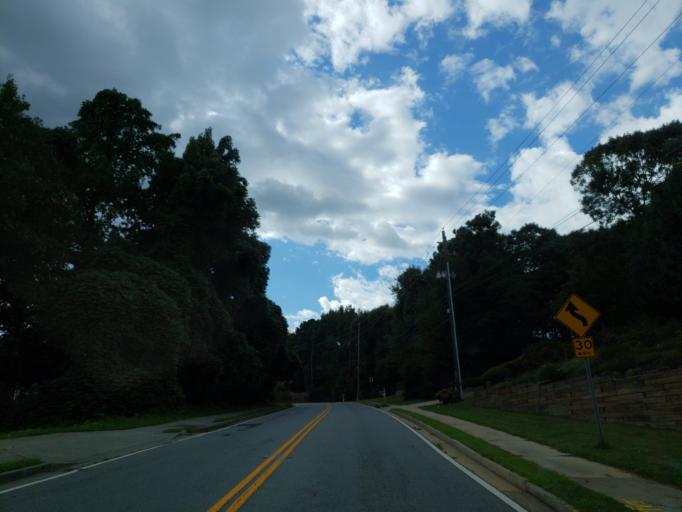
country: US
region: Georgia
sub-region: Cobb County
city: Kennesaw
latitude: 34.0570
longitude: -84.5815
